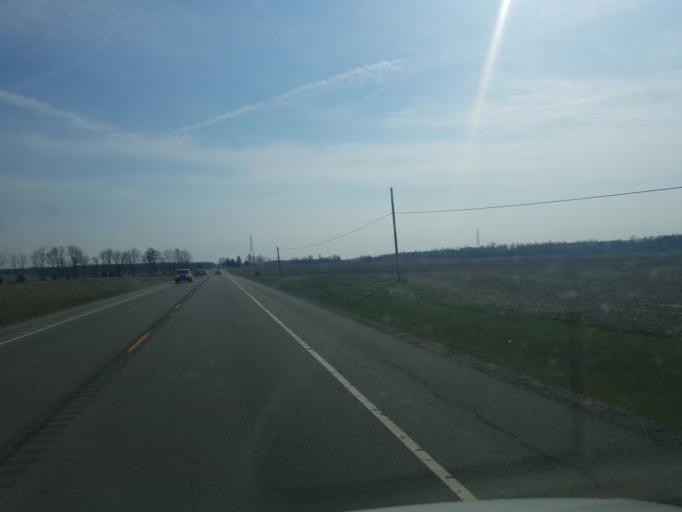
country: US
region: Ohio
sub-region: Logan County
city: Northwood
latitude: 40.5518
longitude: -83.6663
